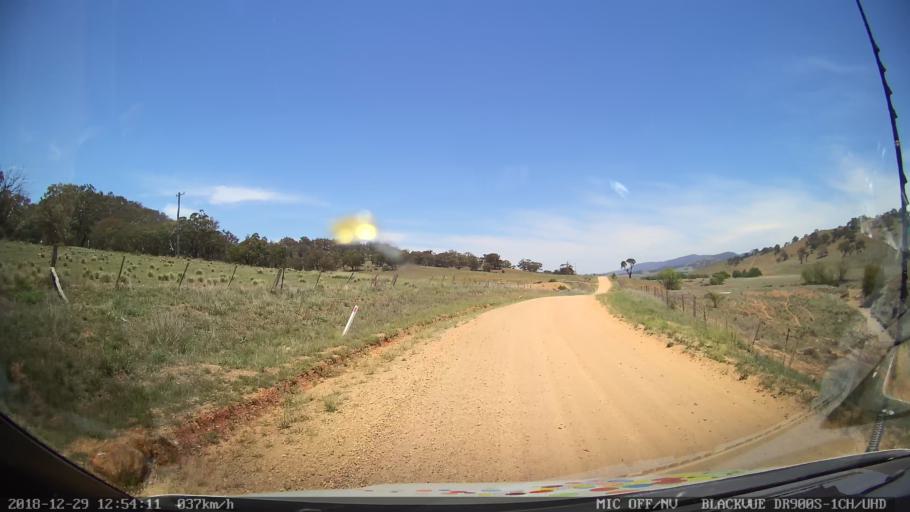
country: AU
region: Australian Capital Territory
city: Macarthur
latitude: -35.6898
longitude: 149.1873
